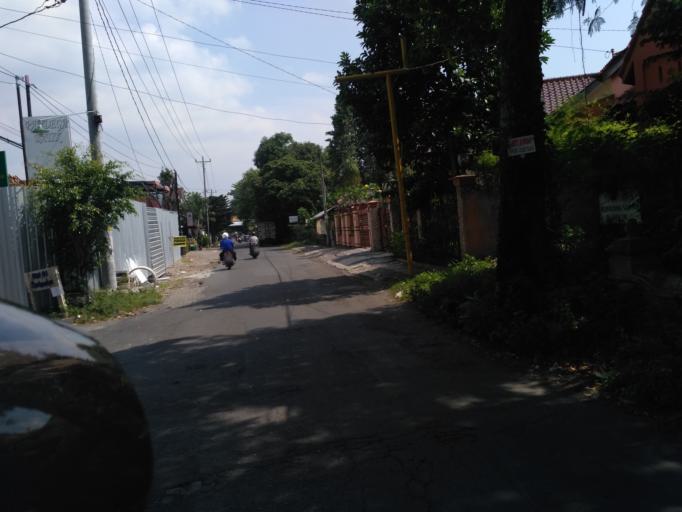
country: ID
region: Daerah Istimewa Yogyakarta
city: Melati
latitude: -7.7549
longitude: 110.3806
